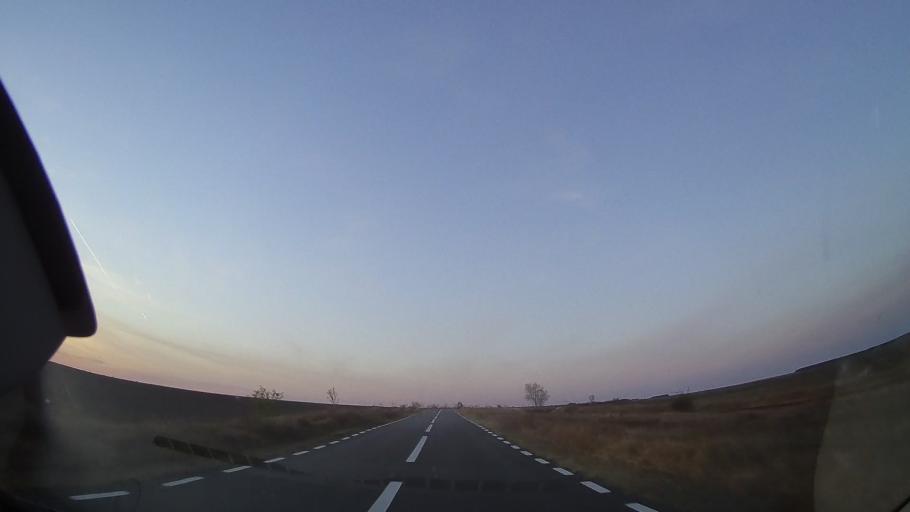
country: RO
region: Constanta
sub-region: Comuna Cobadin
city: Cobadin
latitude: 44.0255
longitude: 28.2649
